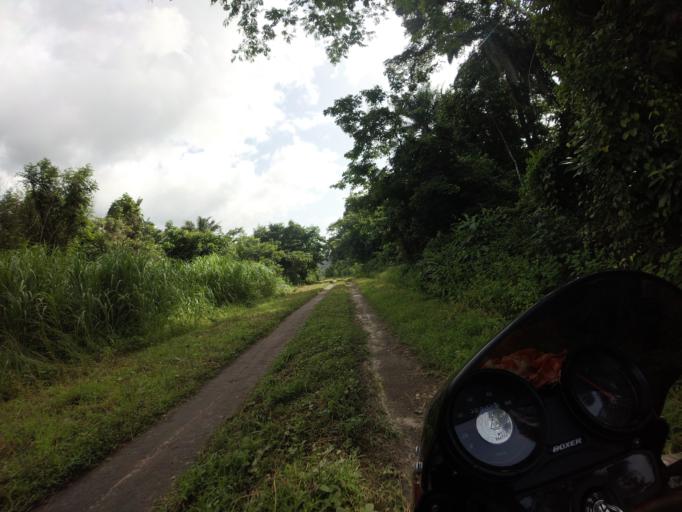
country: SL
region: Eastern Province
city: Tombu
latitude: 8.5317
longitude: -10.7407
